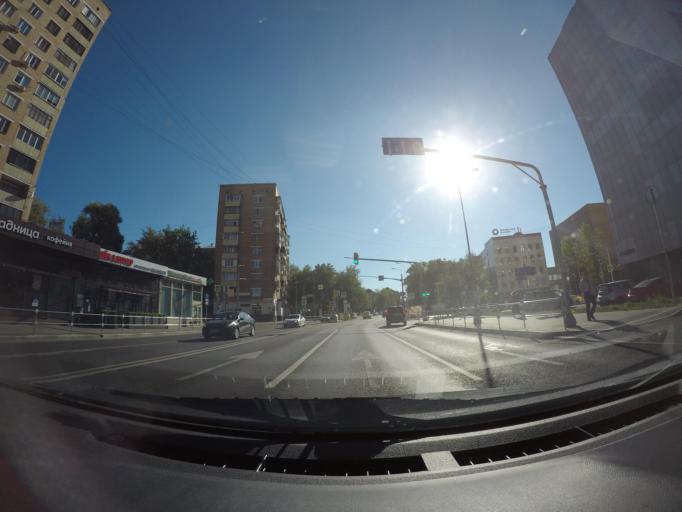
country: RU
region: Moscow
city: Lefortovo
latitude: 55.7821
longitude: 37.7087
